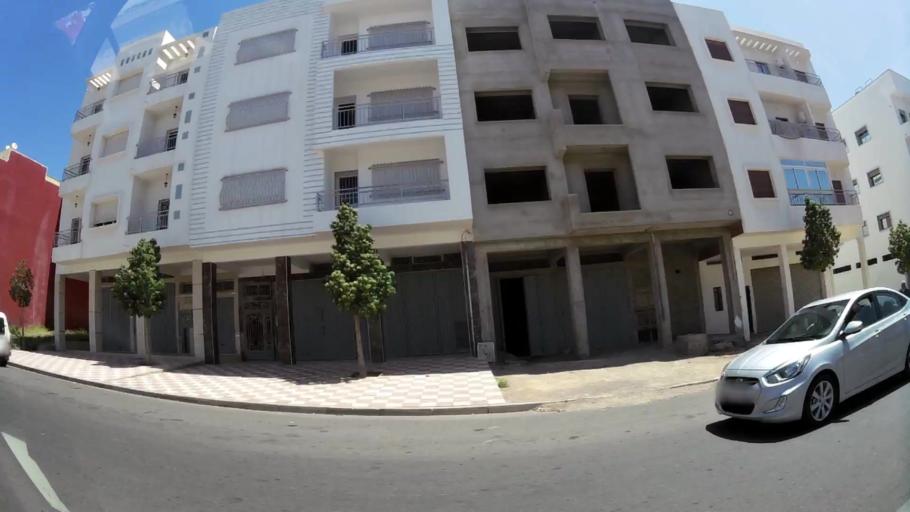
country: MA
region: Oued ed Dahab-Lagouira
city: Dakhla
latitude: 30.4318
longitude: -9.5563
